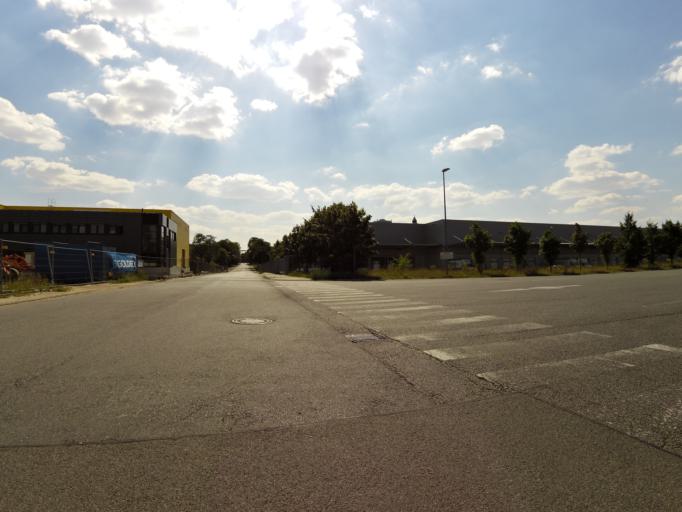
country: DE
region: Berlin
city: Mariendorf
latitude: 52.4414
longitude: 13.3713
